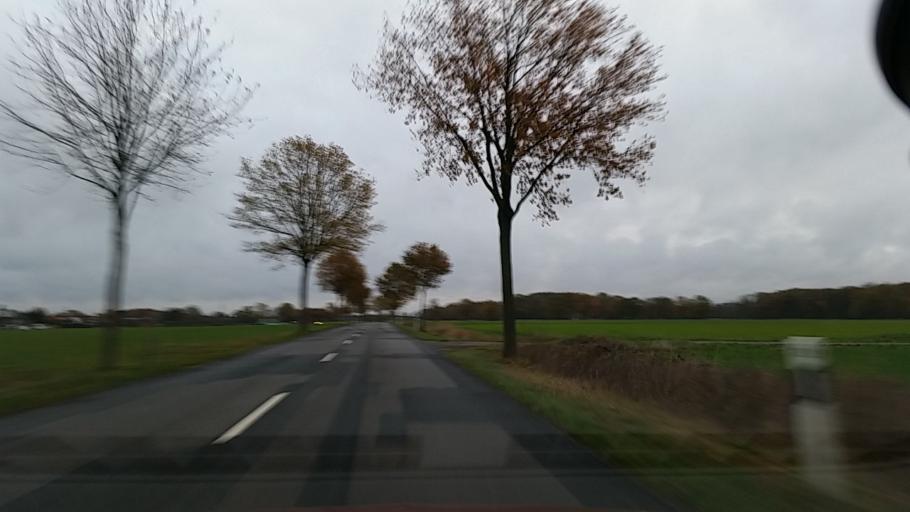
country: DE
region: Lower Saxony
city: Barwedel
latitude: 52.4992
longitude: 10.7881
